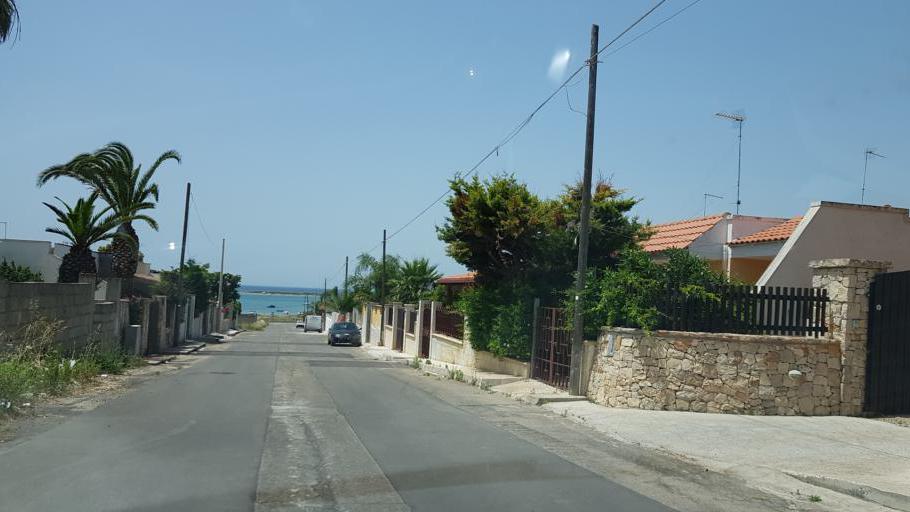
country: IT
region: Apulia
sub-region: Provincia di Lecce
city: Porto Cesareo
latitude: 40.2526
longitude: 17.9111
